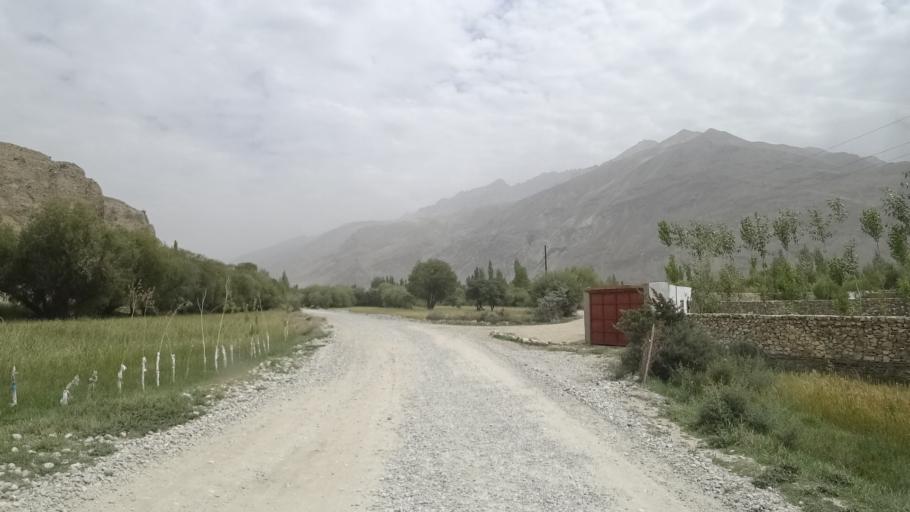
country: AF
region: Badakhshan
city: Khandud
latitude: 37.0414
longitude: 72.6624
